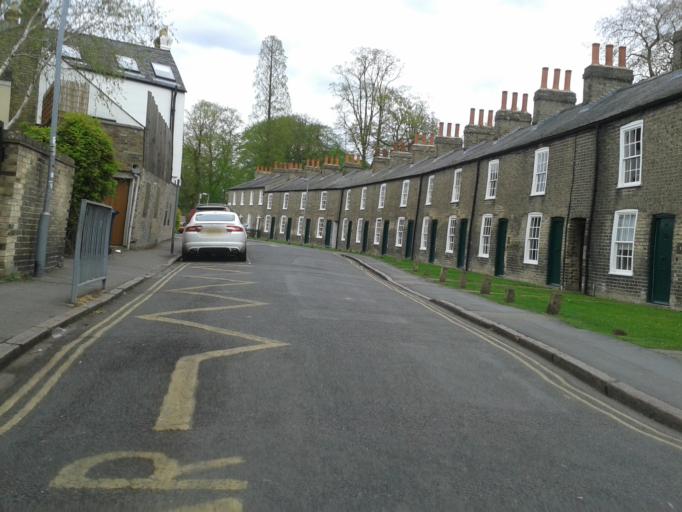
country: GB
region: England
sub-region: Cambridgeshire
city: Cambridge
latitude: 52.2099
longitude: 0.1201
